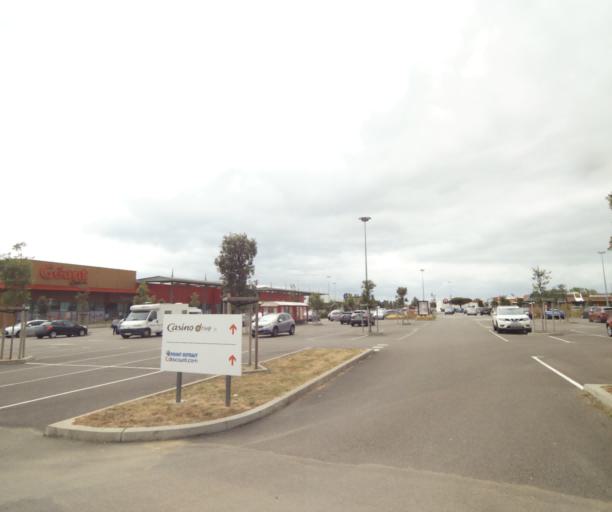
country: FR
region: Pays de la Loire
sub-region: Departement de la Vendee
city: Chateau-d'Olonne
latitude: 46.4874
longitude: -1.7463
